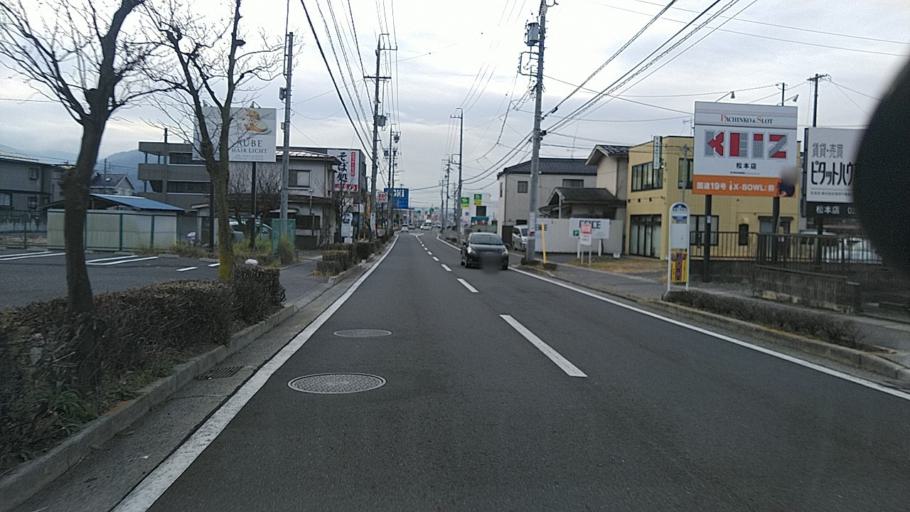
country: JP
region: Nagano
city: Matsumoto
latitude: 36.2238
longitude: 137.9797
